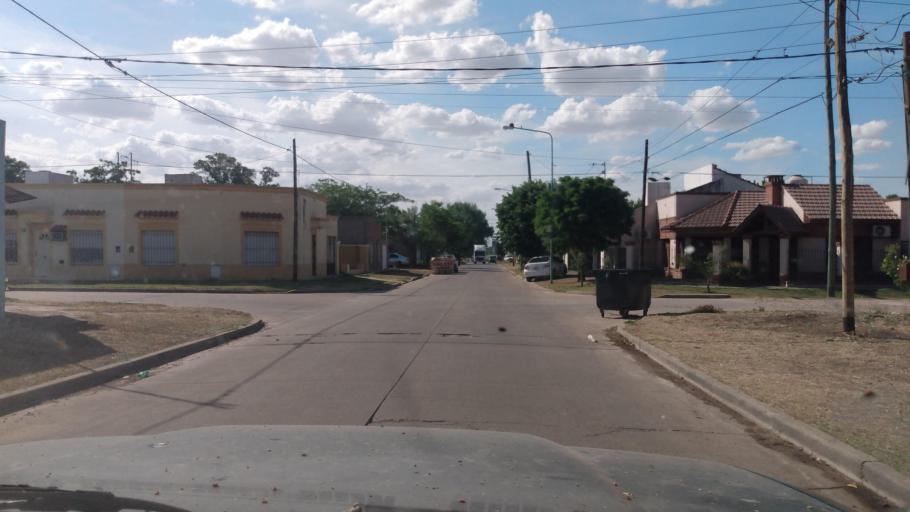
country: AR
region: Buenos Aires
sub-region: Partido de Lujan
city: Lujan
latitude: -34.5541
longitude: -59.1095
